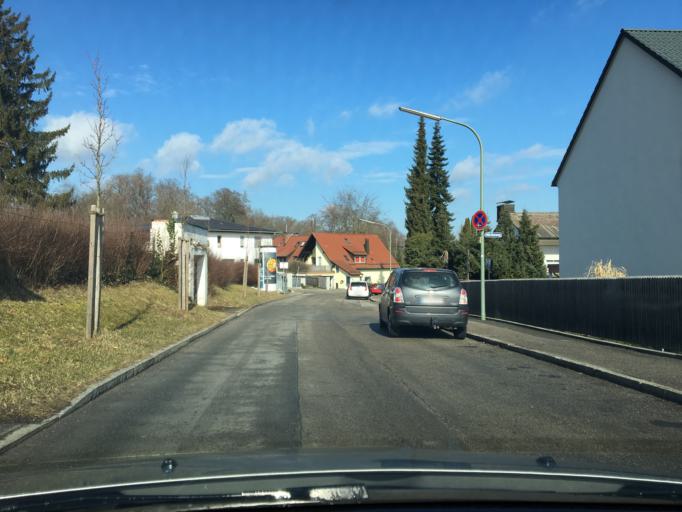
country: DE
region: Bavaria
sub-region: Lower Bavaria
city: Landshut
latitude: 48.5315
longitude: 12.1649
